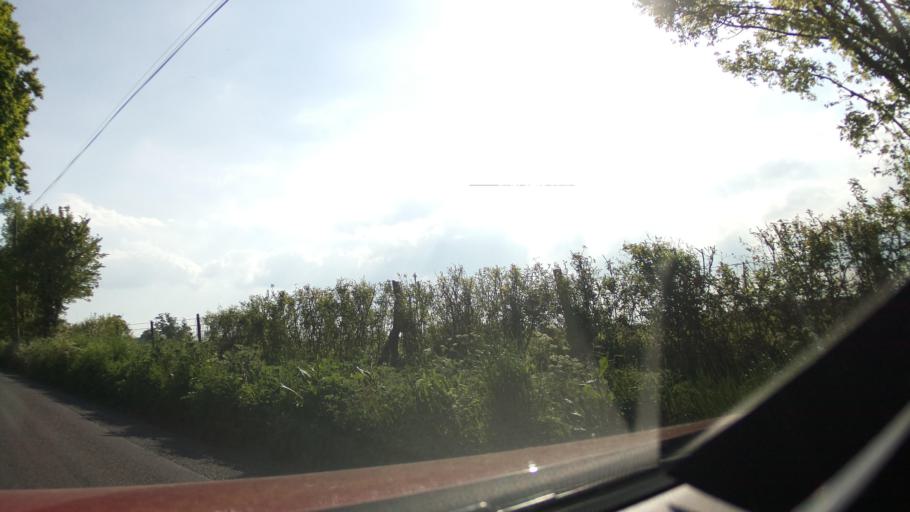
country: GB
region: England
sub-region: Wiltshire
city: Biddestone
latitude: 51.4785
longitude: -2.1757
